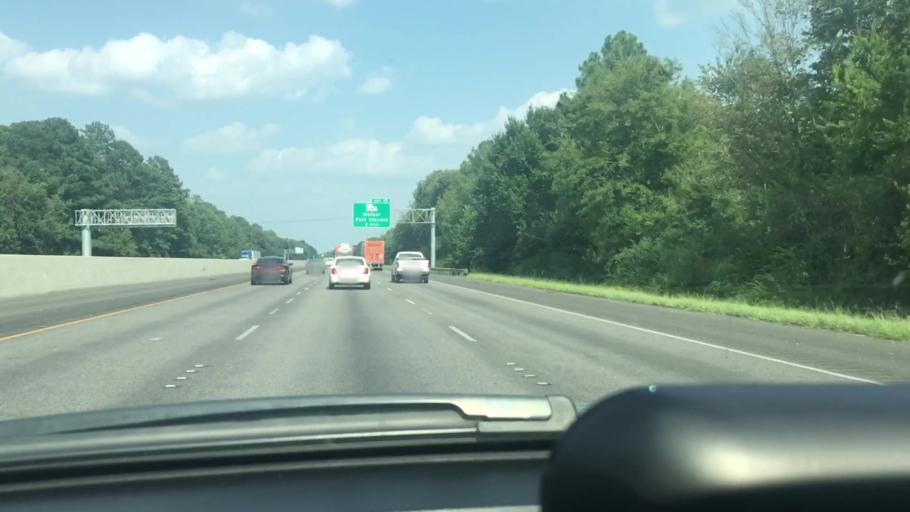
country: US
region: Louisiana
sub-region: Livingston Parish
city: Walker
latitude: 30.4658
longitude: -90.9015
